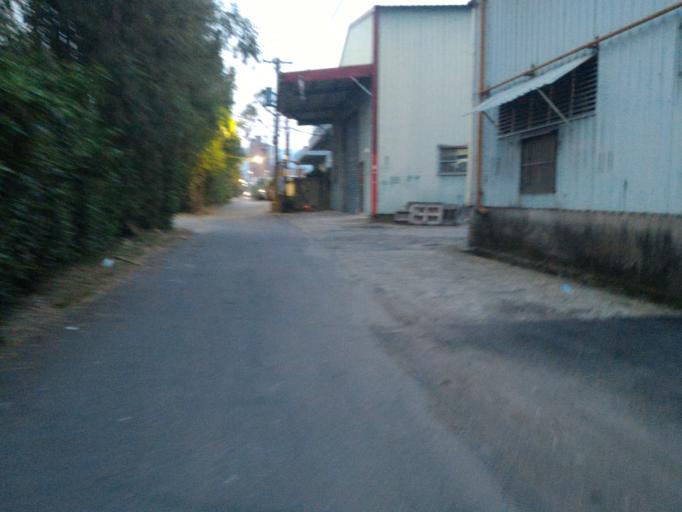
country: TW
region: Taipei
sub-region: Taipei
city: Banqiao
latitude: 24.9568
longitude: 121.4027
